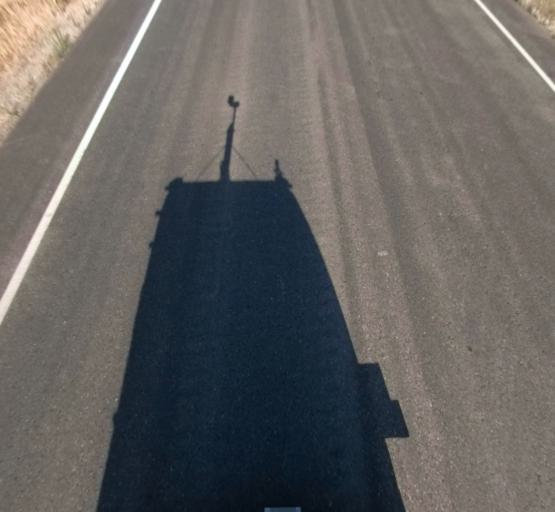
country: US
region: California
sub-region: Madera County
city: Parksdale
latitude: 36.9668
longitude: -119.9848
